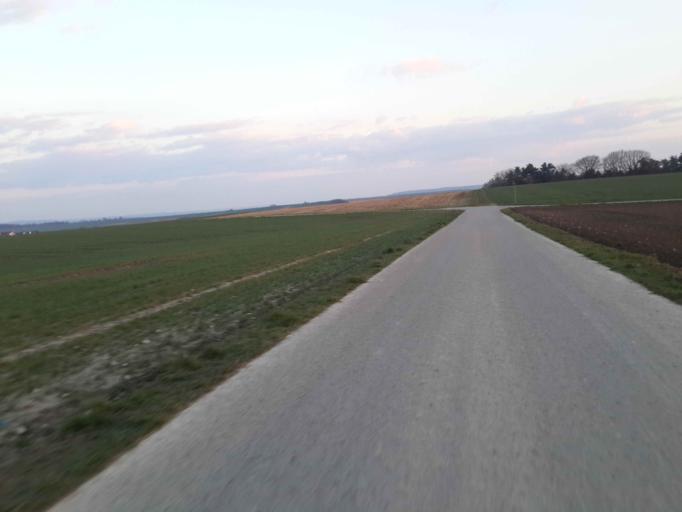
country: DE
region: Baden-Wuerttemberg
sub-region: Regierungsbezirk Stuttgart
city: Bad Rappenau
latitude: 49.2260
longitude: 9.0730
